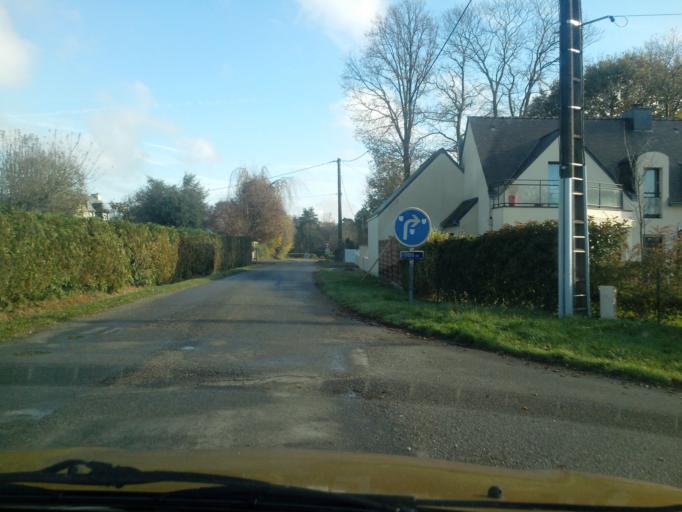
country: FR
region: Brittany
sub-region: Departement du Morbihan
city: Molac
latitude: 47.7297
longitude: -2.4441
